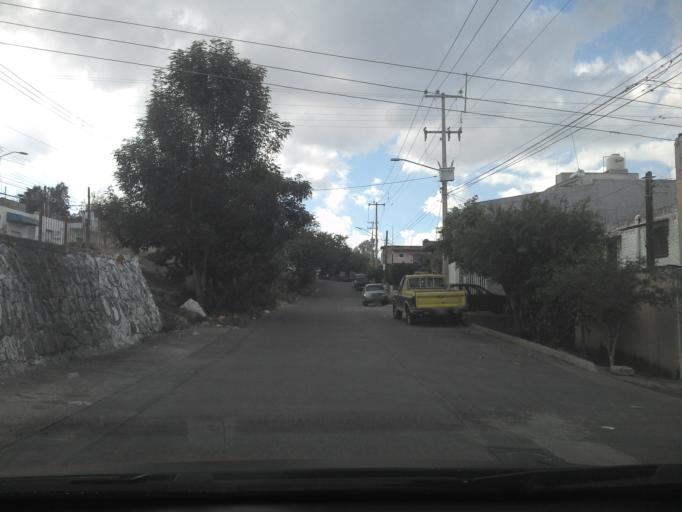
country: MX
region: Jalisco
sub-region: Tlajomulco de Zuniga
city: Altus Bosques
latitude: 20.6162
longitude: -103.3699
